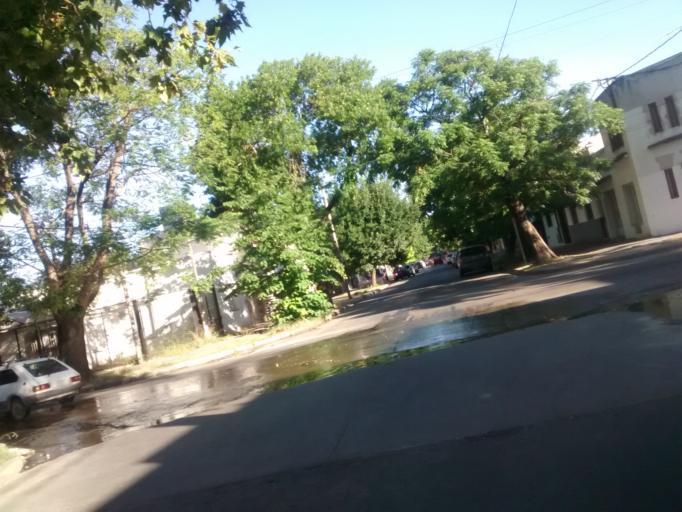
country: AR
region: Buenos Aires
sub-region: Partido de La Plata
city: La Plata
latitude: -34.9369
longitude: -57.9407
